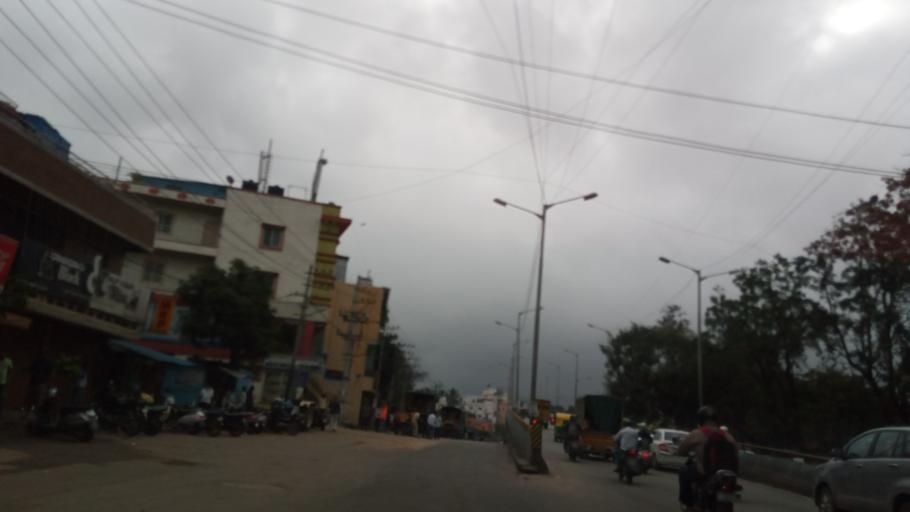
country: IN
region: Karnataka
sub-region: Bangalore Urban
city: Bangalore
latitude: 12.9348
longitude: 77.5375
